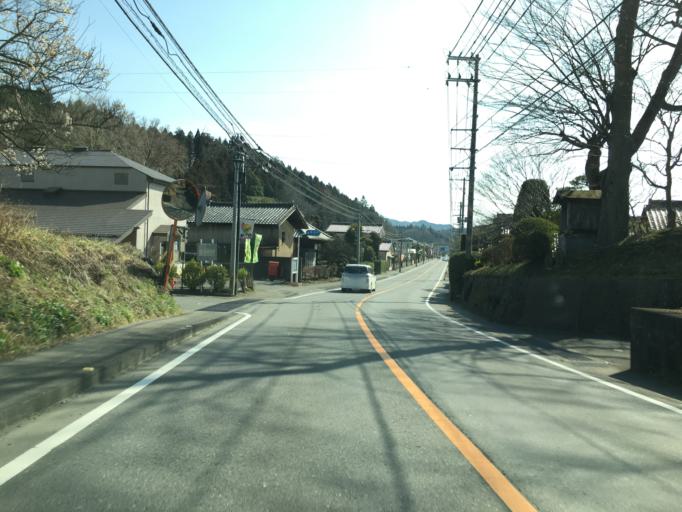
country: JP
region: Ibaraki
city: Daigo
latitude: 36.8770
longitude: 140.4236
